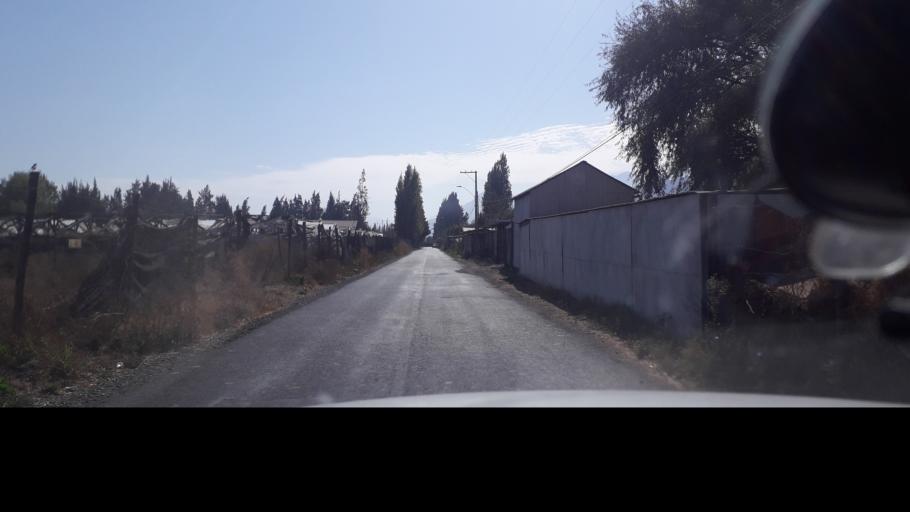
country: CL
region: Valparaiso
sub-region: Provincia de San Felipe
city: Llaillay
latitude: -32.8548
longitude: -70.9411
